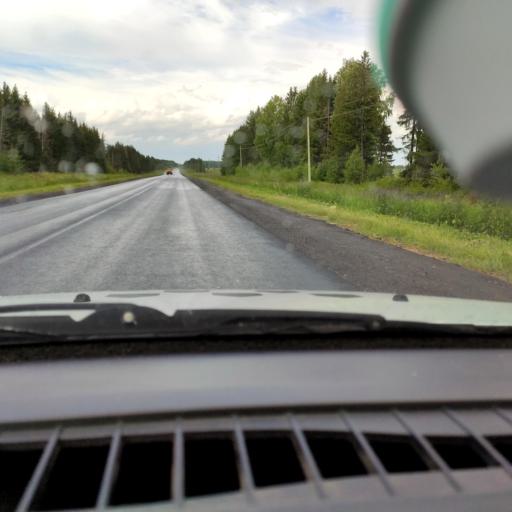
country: RU
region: Perm
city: Orda
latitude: 57.2112
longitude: 56.9353
